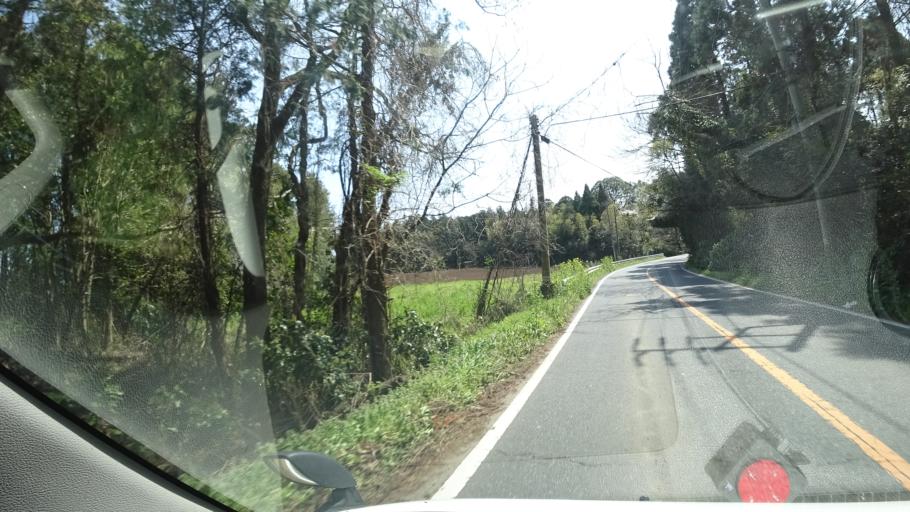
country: JP
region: Chiba
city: Narita
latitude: 35.7353
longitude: 140.3840
